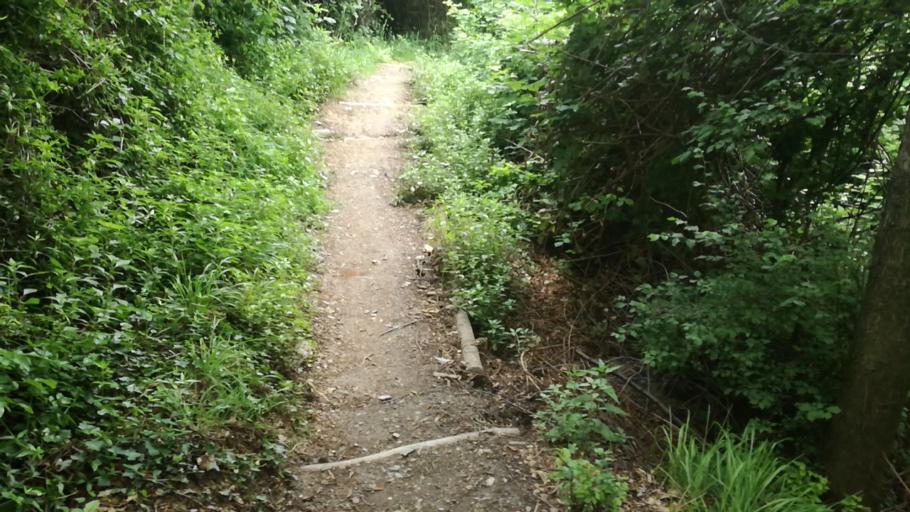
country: IT
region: Liguria
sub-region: Provincia di Genova
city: San Teodoro
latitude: 44.4248
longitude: 8.8972
